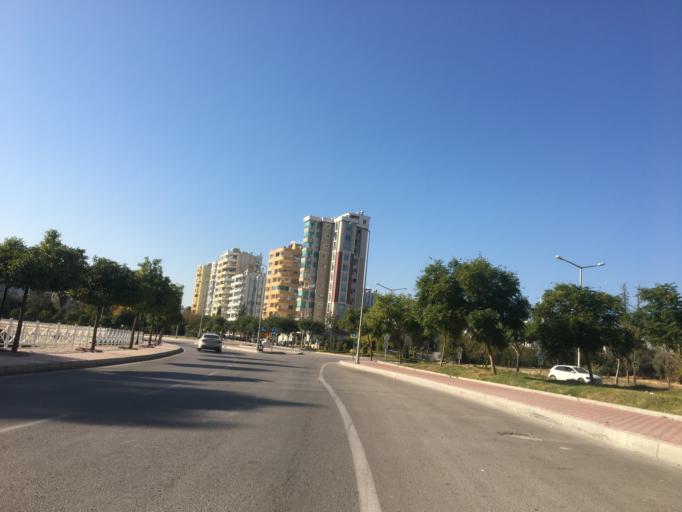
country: TR
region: Adana
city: Seyhan
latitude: 37.0285
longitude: 35.2712
